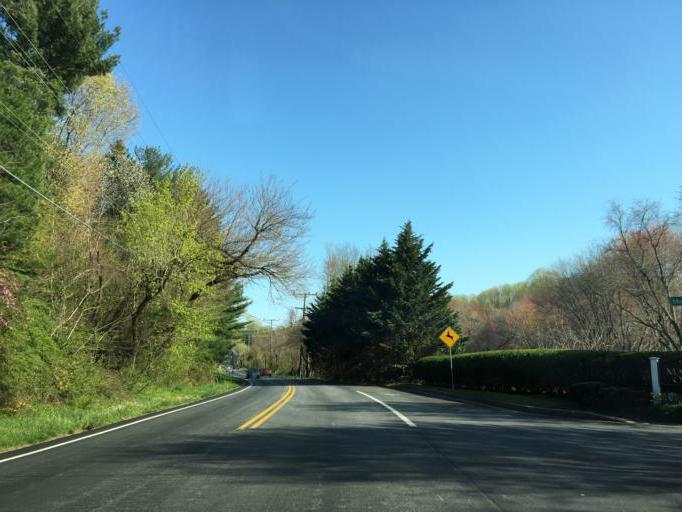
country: US
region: Maryland
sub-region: Baltimore County
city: Hampton
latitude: 39.5054
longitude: -76.5352
